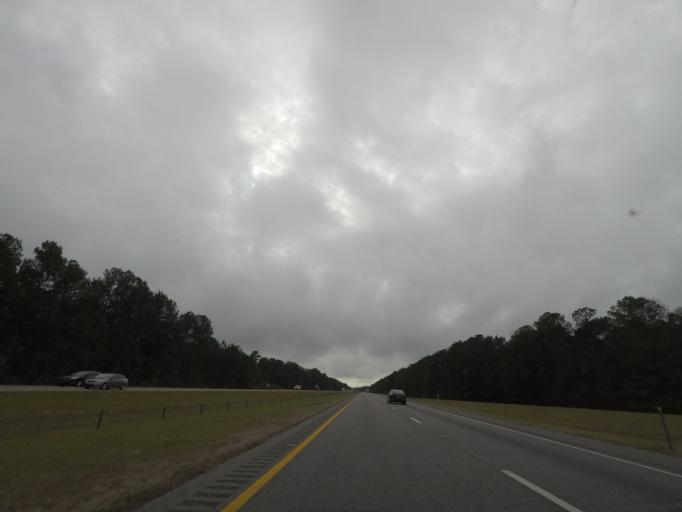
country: US
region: South Carolina
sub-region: Orangeburg County
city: Holly Hill
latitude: 33.4111
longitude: -80.5005
